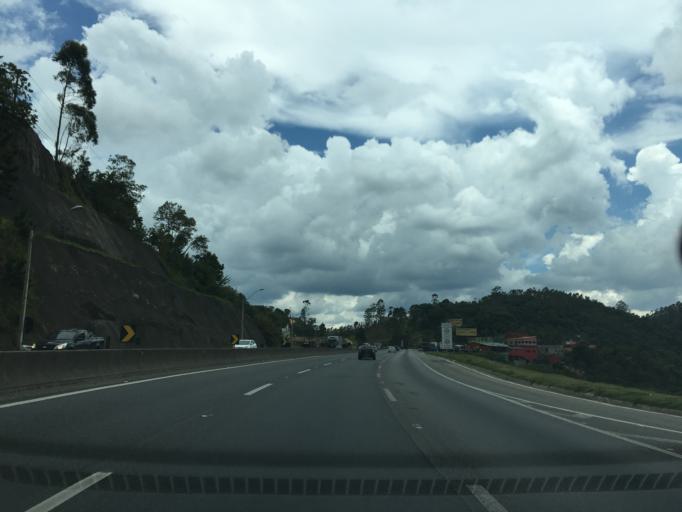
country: BR
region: Sao Paulo
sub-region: Mairipora
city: Mairipora
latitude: -23.2849
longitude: -46.5898
